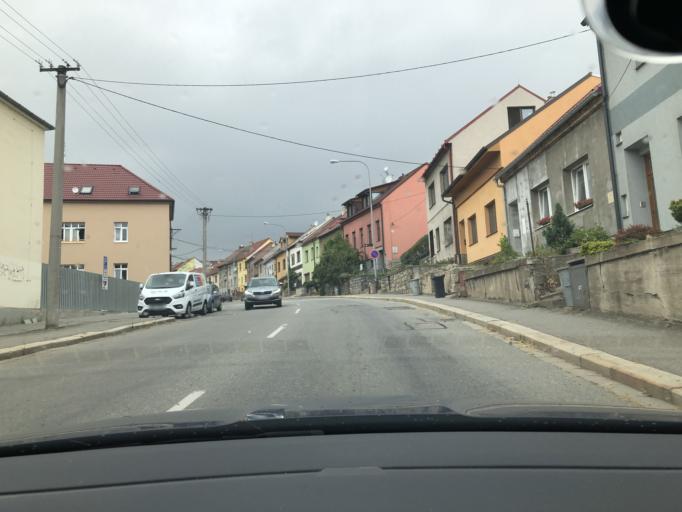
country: CZ
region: Vysocina
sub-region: Okres Trebic
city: Trebic
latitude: 49.2182
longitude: 15.8719
